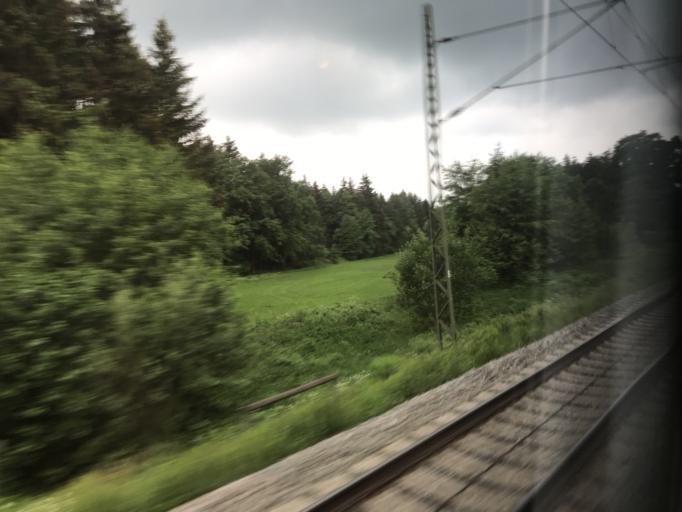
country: DE
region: Bavaria
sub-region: Swabia
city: Ustersbach
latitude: 48.3334
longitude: 10.6411
